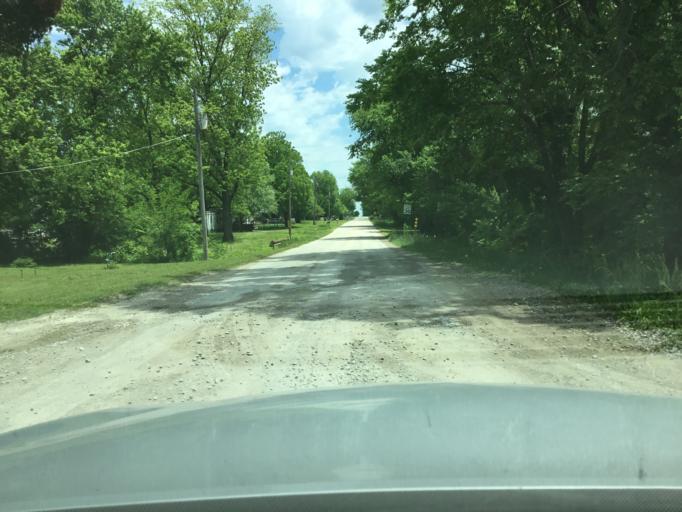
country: US
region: Kansas
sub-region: Montgomery County
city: Independence
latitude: 37.1095
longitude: -95.7650
